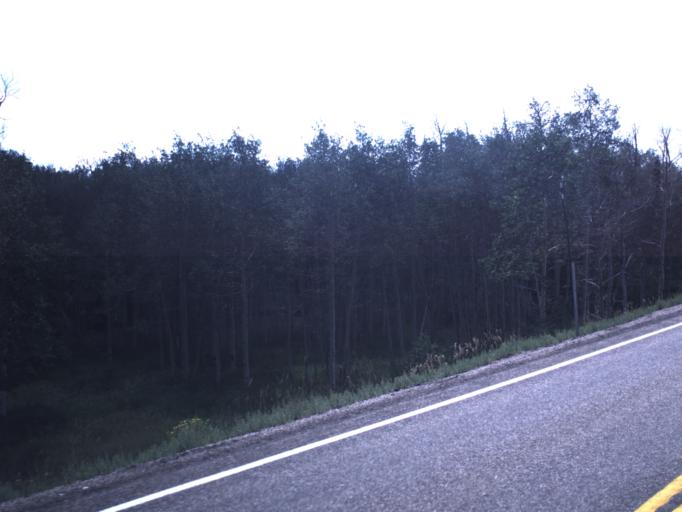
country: US
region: Utah
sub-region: Uintah County
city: Maeser
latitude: 40.6955
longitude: -109.4931
